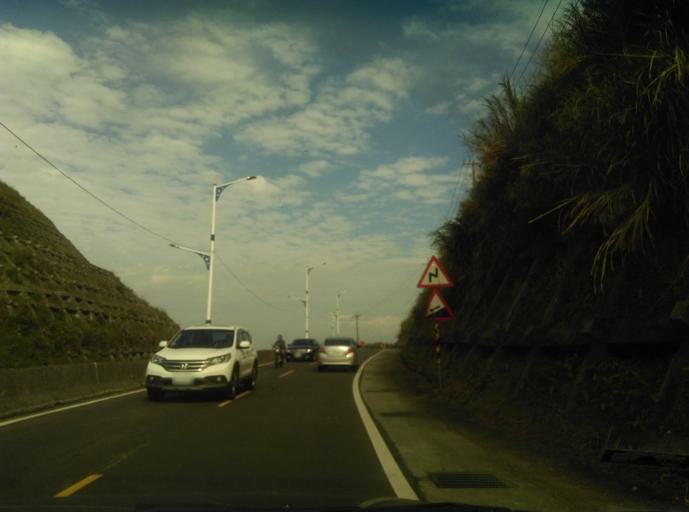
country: TW
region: Taiwan
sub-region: Keelung
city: Keelung
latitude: 25.1625
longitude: 121.7020
